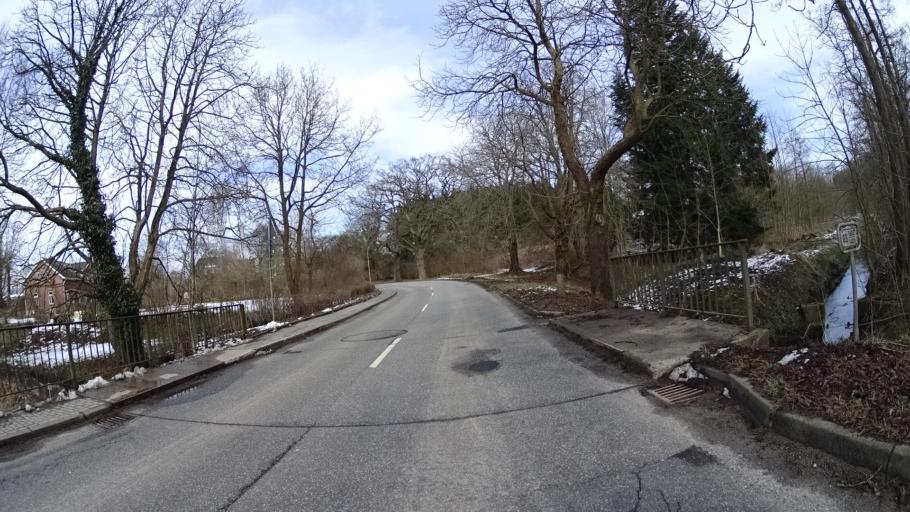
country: DE
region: Schleswig-Holstein
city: Kuhren
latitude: 54.1995
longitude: 10.2603
